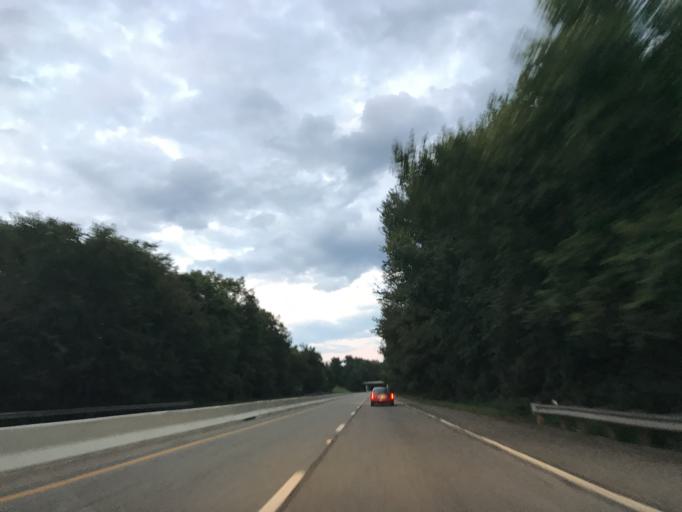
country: US
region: Ohio
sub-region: Columbiana County
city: Glenmoor
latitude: 40.6740
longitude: -80.6150
